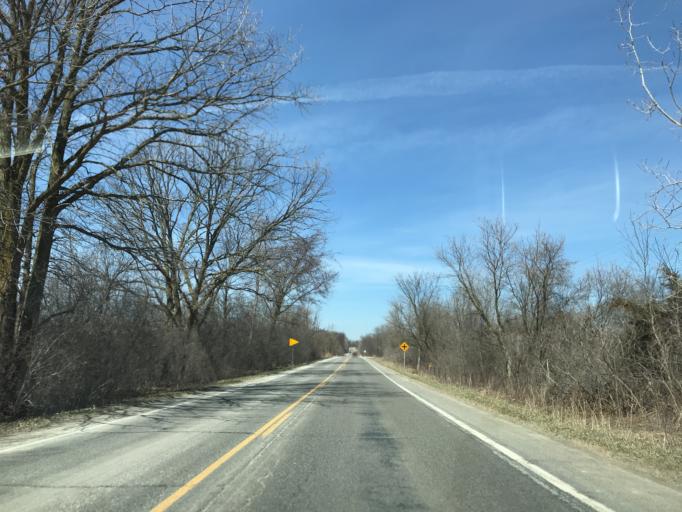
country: US
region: Michigan
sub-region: Washtenaw County
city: Ann Arbor
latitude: 42.3298
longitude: -83.7081
